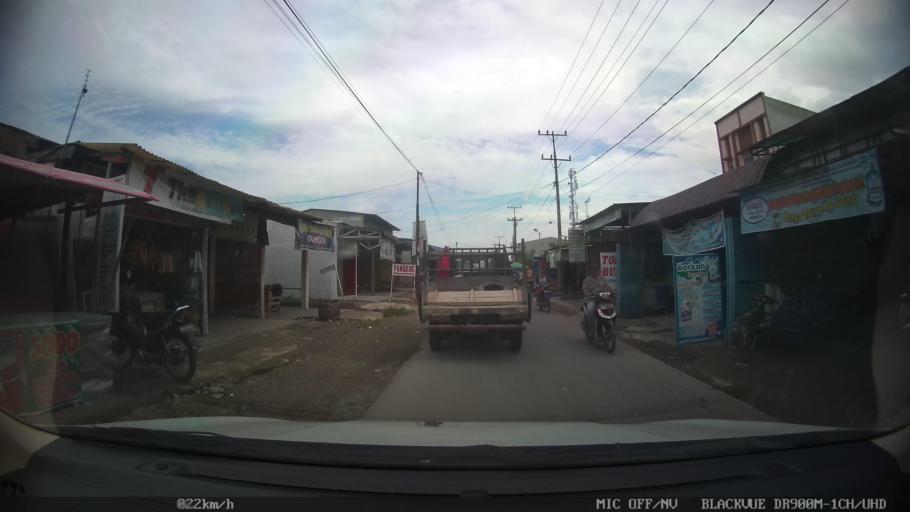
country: ID
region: North Sumatra
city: Sunggal
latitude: 3.6078
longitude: 98.5804
